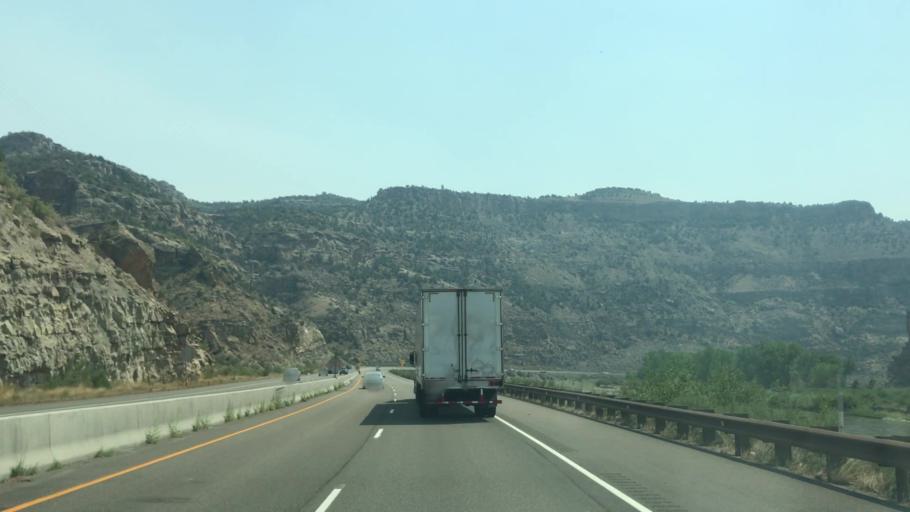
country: US
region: Colorado
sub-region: Mesa County
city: Palisade
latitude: 39.2454
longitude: -108.2563
